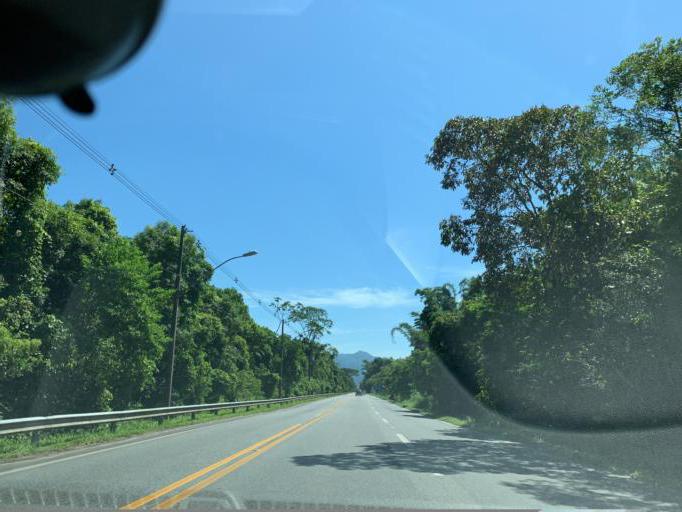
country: BR
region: Sao Paulo
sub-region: Bertioga
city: Bertioga
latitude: -23.7802
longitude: -46.0556
